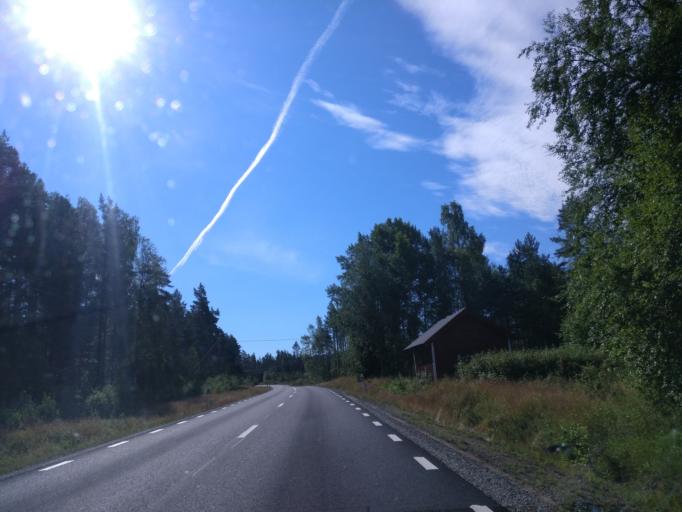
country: SE
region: Vaermland
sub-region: Hagfors Kommun
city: Hagfors
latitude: 60.0597
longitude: 13.7583
